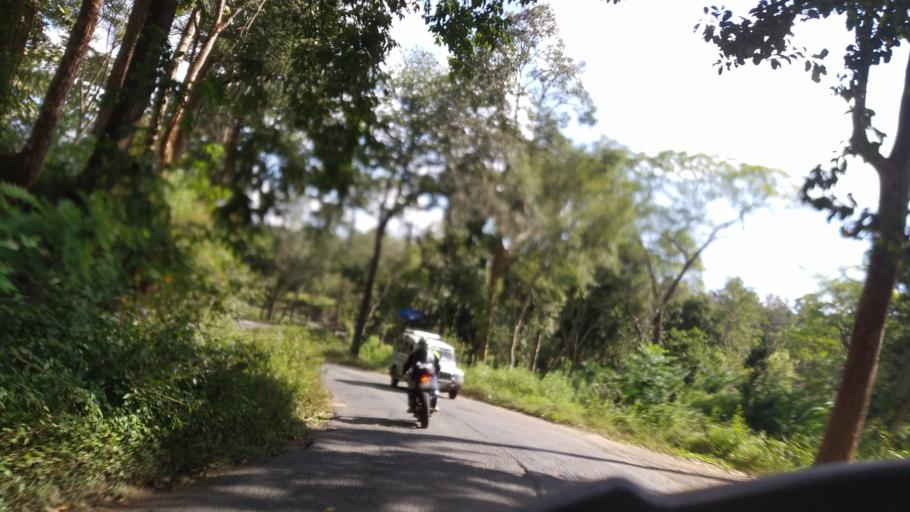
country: IN
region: Kerala
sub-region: Wayanad
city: Panamaram
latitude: 11.9339
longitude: 76.0642
